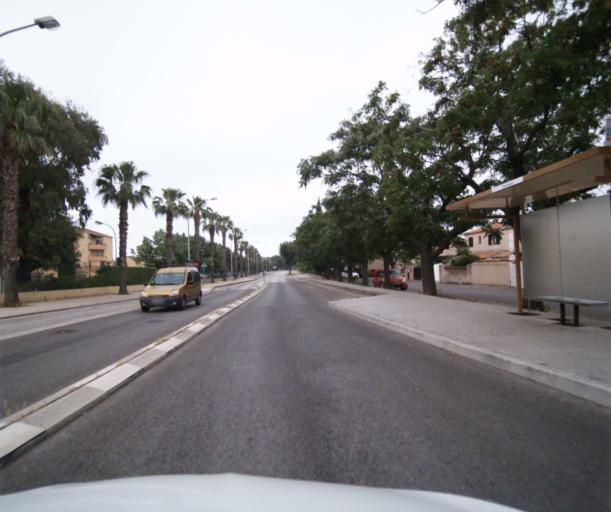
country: FR
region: Provence-Alpes-Cote d'Azur
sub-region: Departement du Var
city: La Seyne-sur-Mer
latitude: 43.0872
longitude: 5.8909
